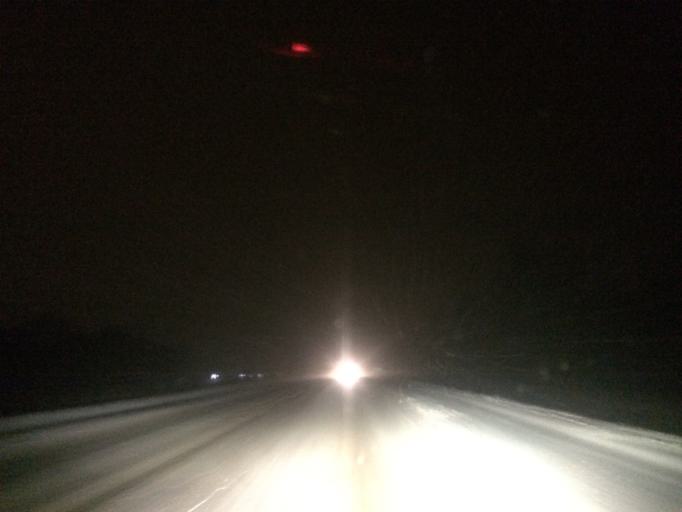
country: RU
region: Tula
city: Kosaya Gora
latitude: 54.1513
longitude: 37.4242
